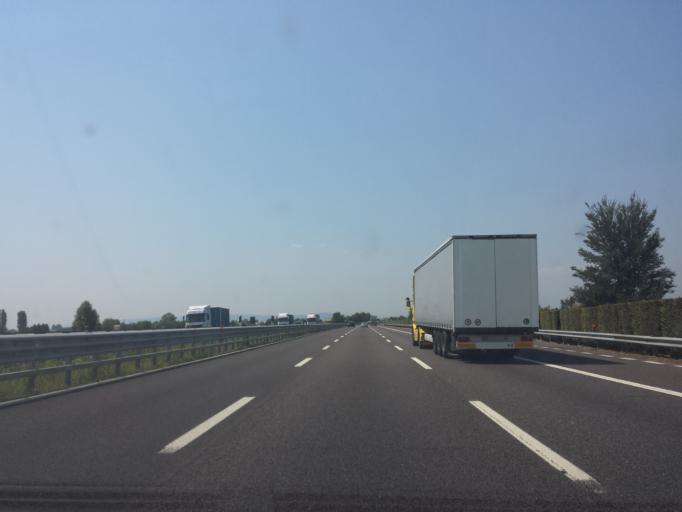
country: IT
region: Veneto
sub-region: Provincia di Padova
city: Bosco
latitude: 45.4553
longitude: 11.7978
